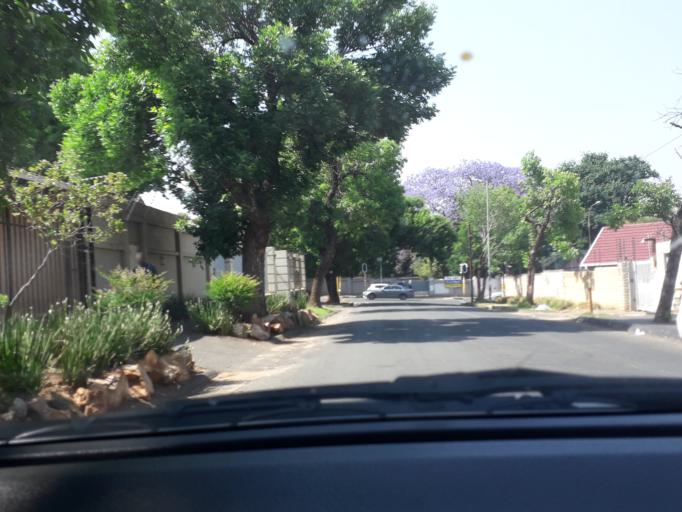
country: ZA
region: Gauteng
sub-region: City of Johannesburg Metropolitan Municipality
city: Johannesburg
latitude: -26.1268
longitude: 28.0773
